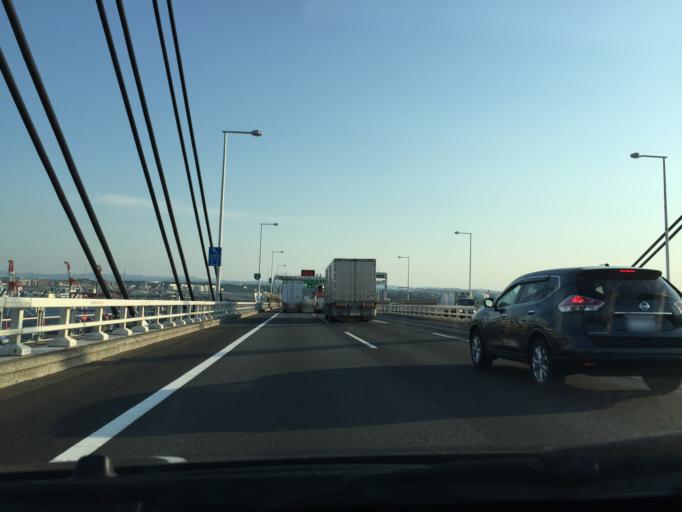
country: JP
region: Kanagawa
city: Yokohama
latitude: 35.4517
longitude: 139.6723
